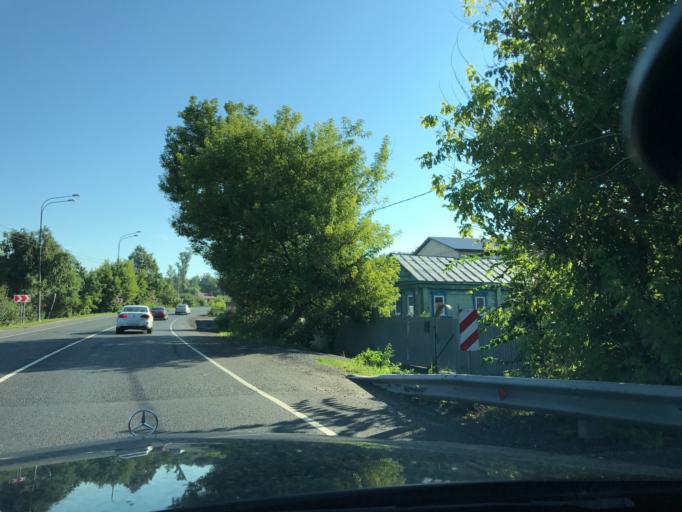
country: RU
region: Moskovskaya
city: Sverdlovskiy
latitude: 55.9252
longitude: 38.1354
